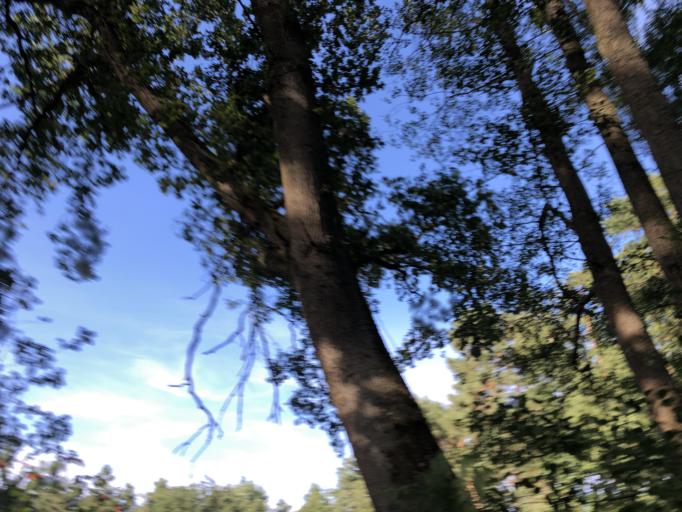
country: DE
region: Lower Saxony
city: Thomasburg
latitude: 53.2117
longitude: 10.6748
